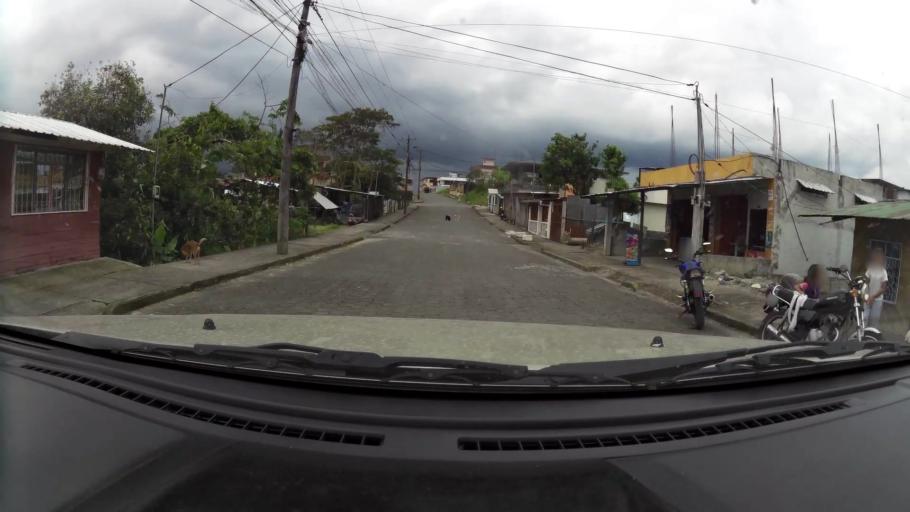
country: EC
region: Pastaza
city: Puyo
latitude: -1.4936
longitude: -78.0042
